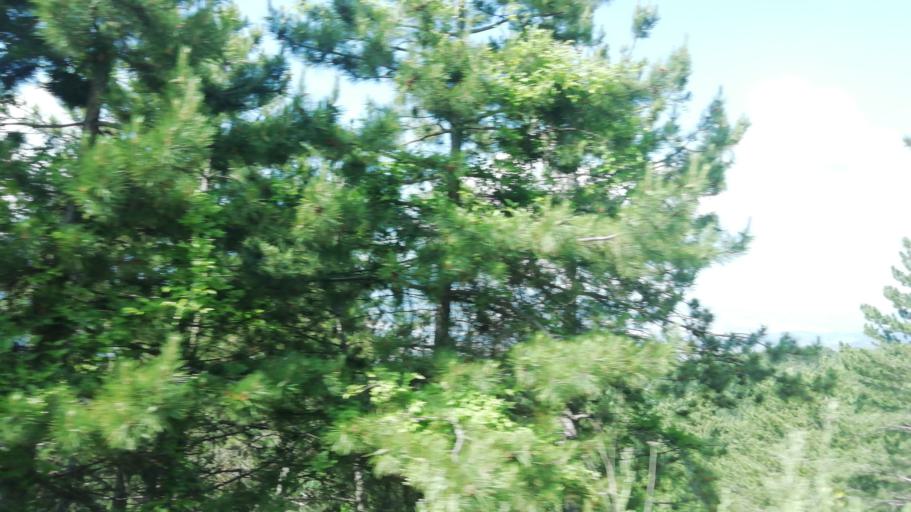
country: TR
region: Karabuk
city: Karabuk
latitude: 41.1247
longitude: 32.5899
